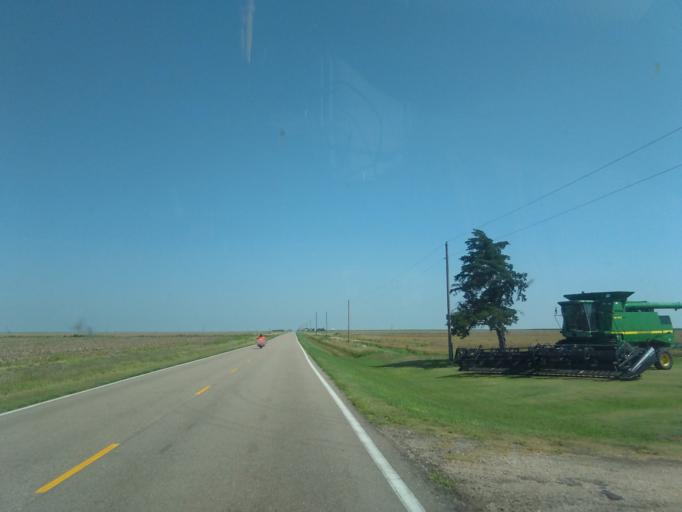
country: US
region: Nebraska
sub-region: Dundy County
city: Benkelman
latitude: 39.7977
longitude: -101.5419
